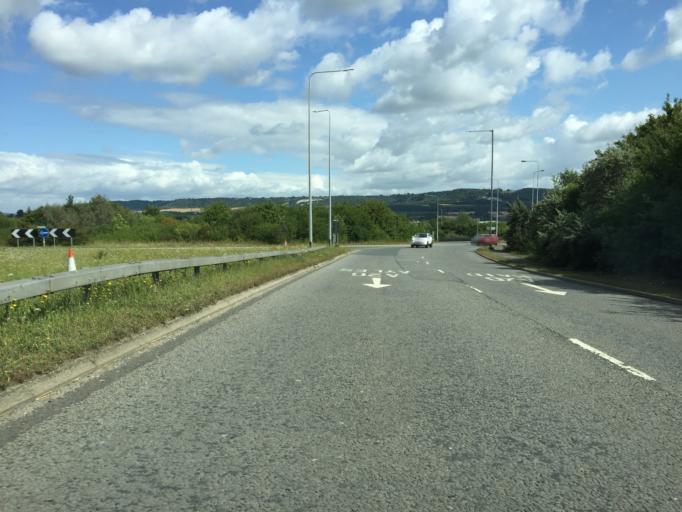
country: GB
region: England
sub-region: Kent
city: Aylesford
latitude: 51.2949
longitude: 0.4845
